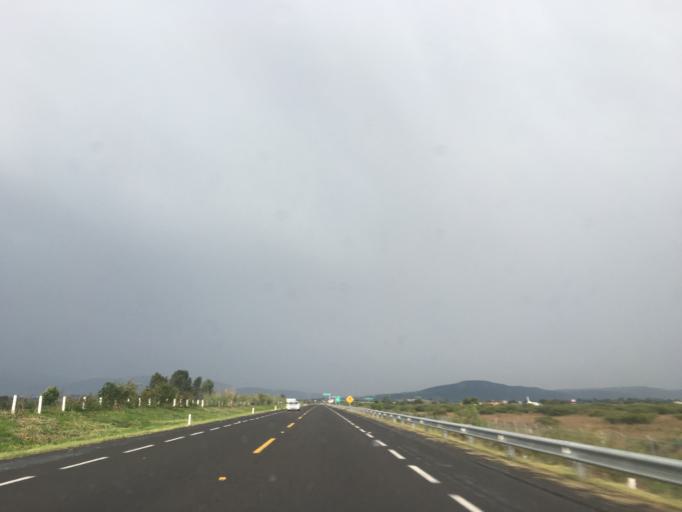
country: MX
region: Michoacan
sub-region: Alvaro Obregon
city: Lazaro Cardenas (La Purisima)
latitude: 19.8616
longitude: -101.0081
